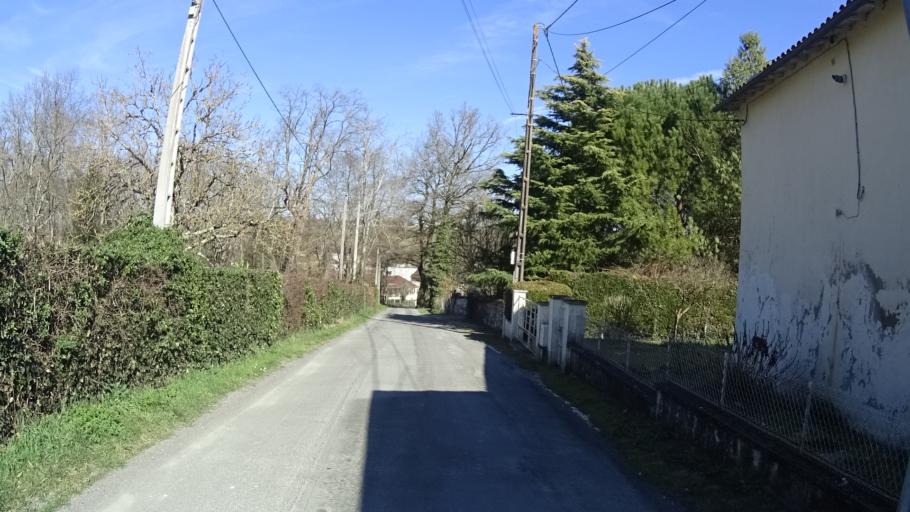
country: FR
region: Aquitaine
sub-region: Departement de la Dordogne
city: Riberac
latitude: 45.2404
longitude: 0.3401
